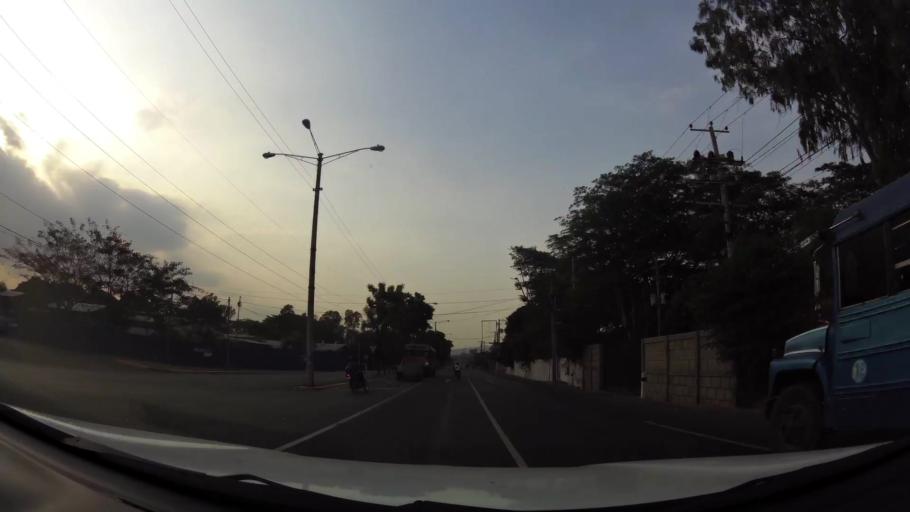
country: NI
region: Managua
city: Ciudad Sandino
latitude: 12.1499
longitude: -86.3364
